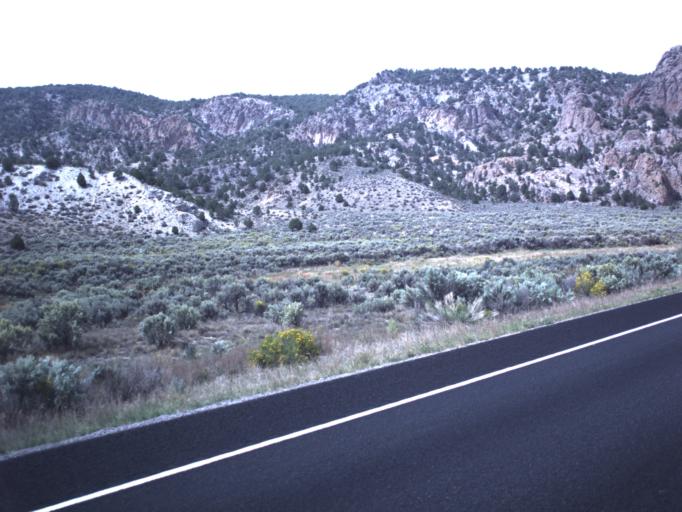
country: US
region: Utah
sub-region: Piute County
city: Junction
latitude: 38.0502
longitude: -112.3534
